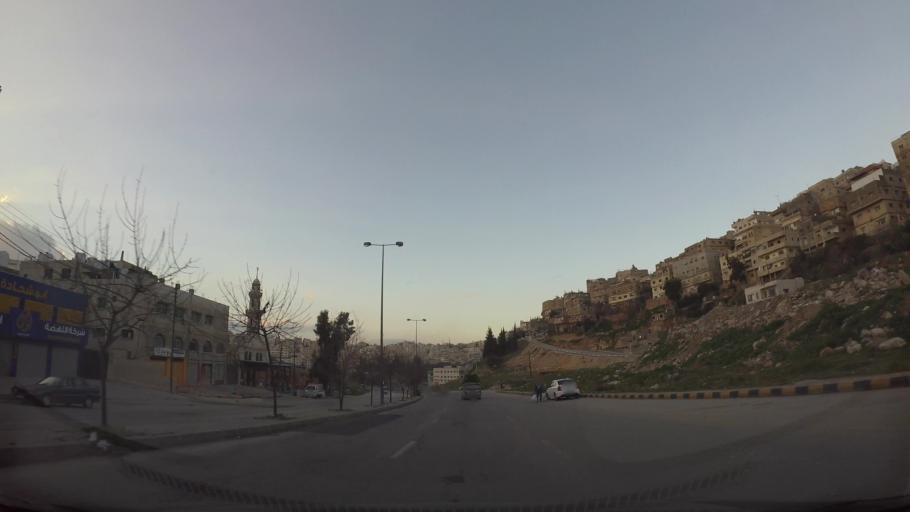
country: JO
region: Amman
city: Al Bunayyat ash Shamaliyah
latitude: 31.9220
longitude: 35.9117
